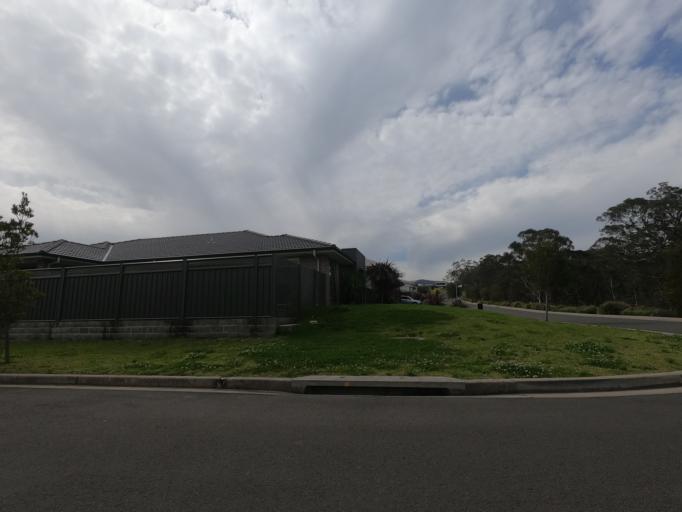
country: AU
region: New South Wales
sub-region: Wollongong
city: Dapto
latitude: -34.4961
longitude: 150.7627
